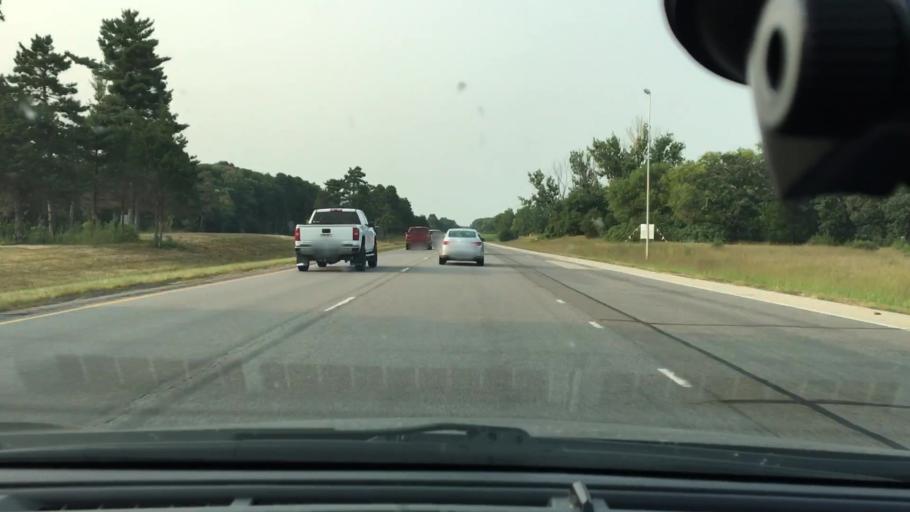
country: US
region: Minnesota
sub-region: Sherburne County
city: Zimmerman
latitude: 45.5050
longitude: -93.5823
